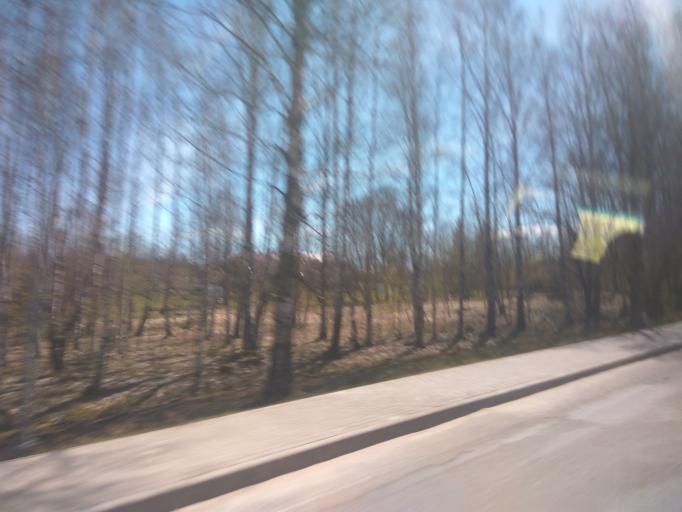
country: LV
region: Aluksnes Rajons
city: Aluksne
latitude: 57.4344
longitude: 27.0389
